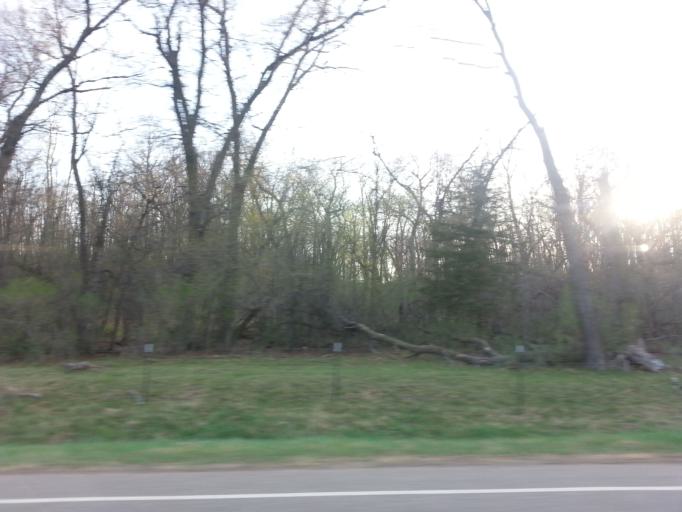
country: US
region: Wisconsin
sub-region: Pierce County
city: River Falls
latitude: 44.8935
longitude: -92.6695
